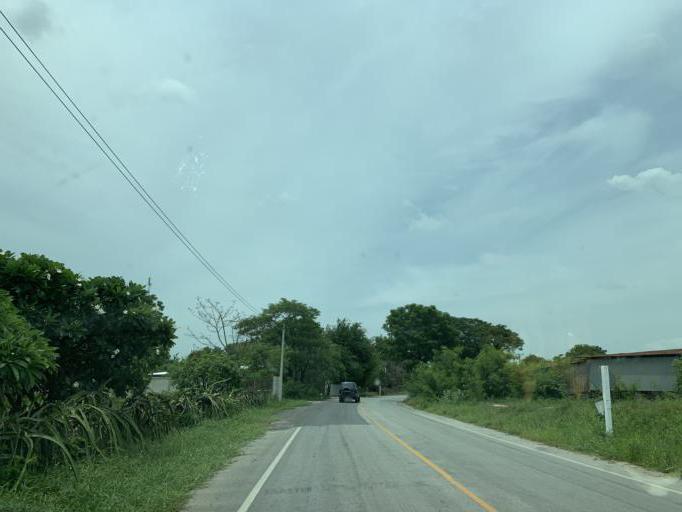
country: TH
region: Uthai Thani
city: Uthai Thani
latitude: 15.4031
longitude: 100.0272
